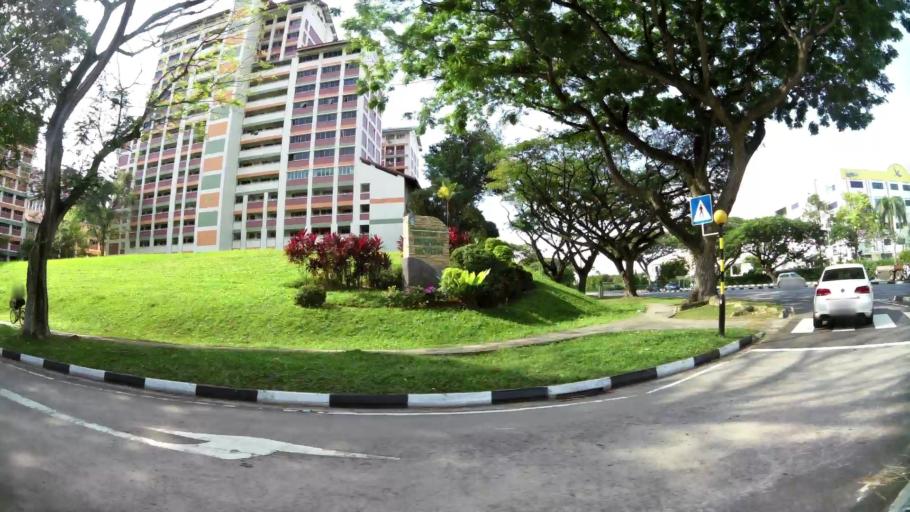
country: SG
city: Singapore
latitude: 1.3606
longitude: 103.8420
